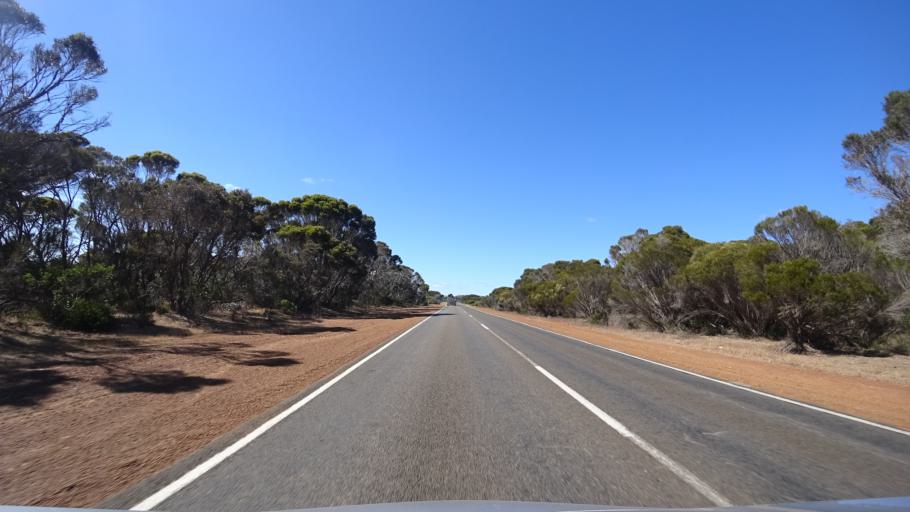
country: AU
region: South Australia
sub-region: Kangaroo Island
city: Kingscote
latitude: -35.7231
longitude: 137.5601
